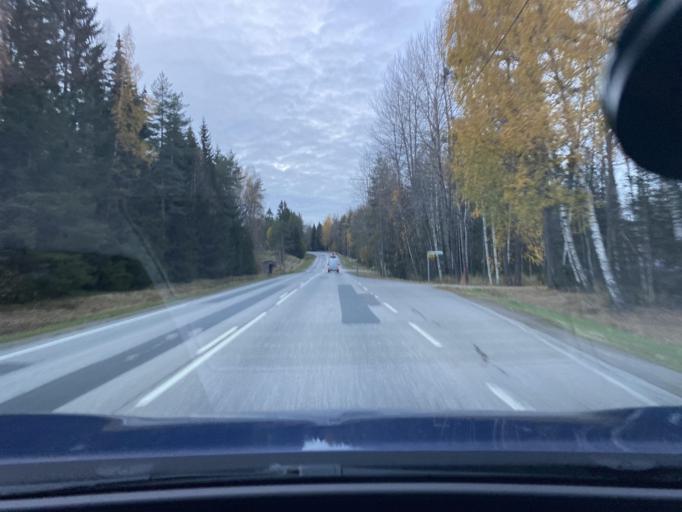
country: FI
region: Uusimaa
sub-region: Helsinki
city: Vihti
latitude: 60.3312
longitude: 24.2100
